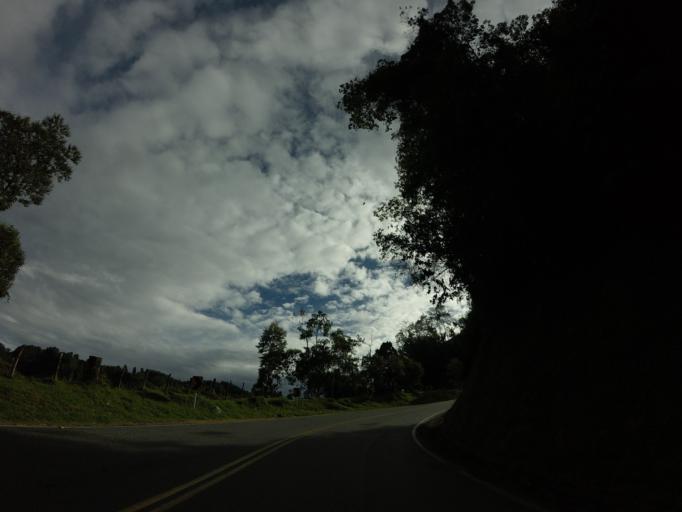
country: CO
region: Tolima
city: Herveo
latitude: 5.1374
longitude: -75.1838
